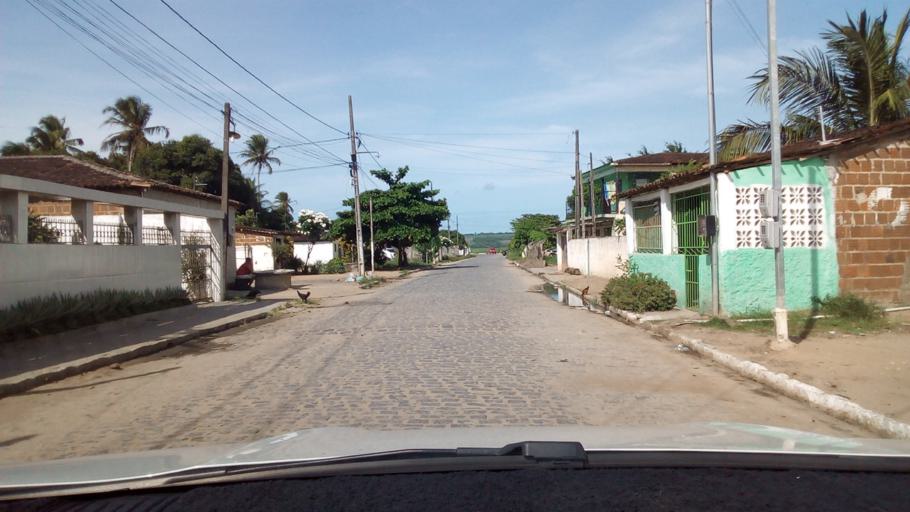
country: BR
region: Paraiba
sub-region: Santa Rita
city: Santa Rita
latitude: -7.0772
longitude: -34.9587
